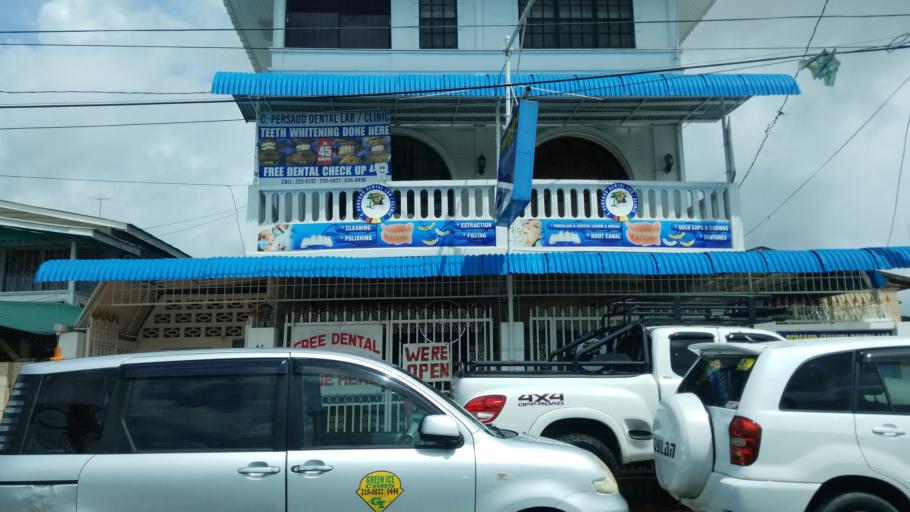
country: GY
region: Demerara-Mahaica
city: Georgetown
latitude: 6.7657
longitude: -58.1774
